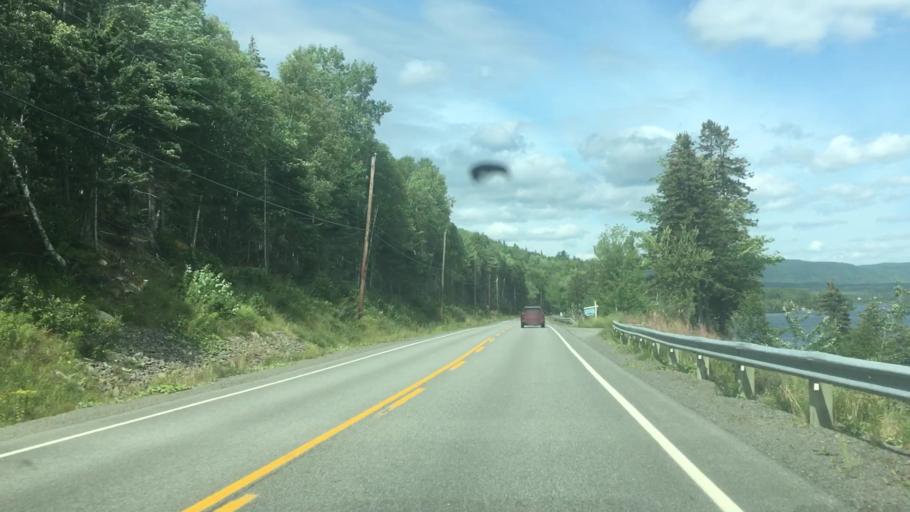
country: CA
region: Nova Scotia
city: Sydney Mines
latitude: 46.2744
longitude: -60.6108
